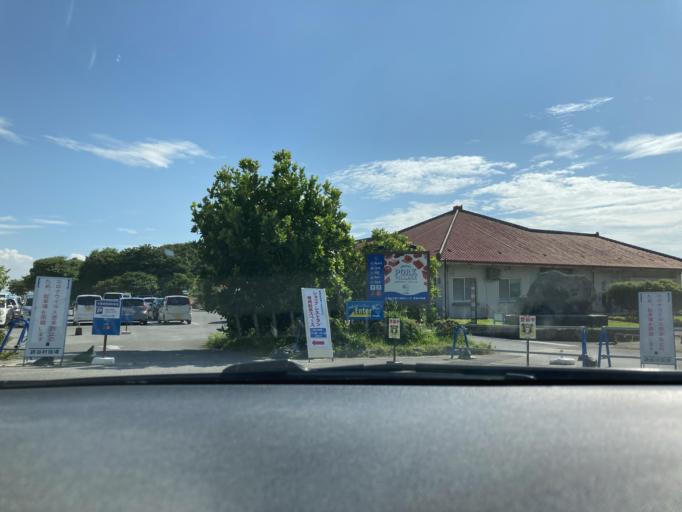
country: JP
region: Okinawa
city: Chatan
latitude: 26.3647
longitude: 127.7387
